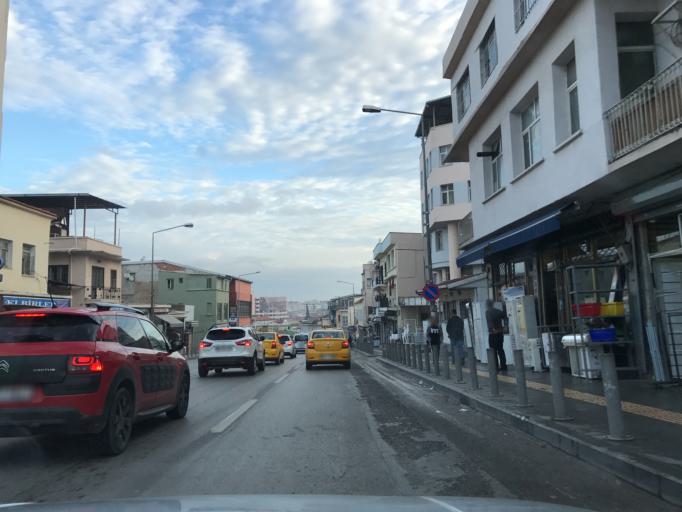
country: TR
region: Izmir
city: Izmir
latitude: 38.4169
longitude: 27.1358
